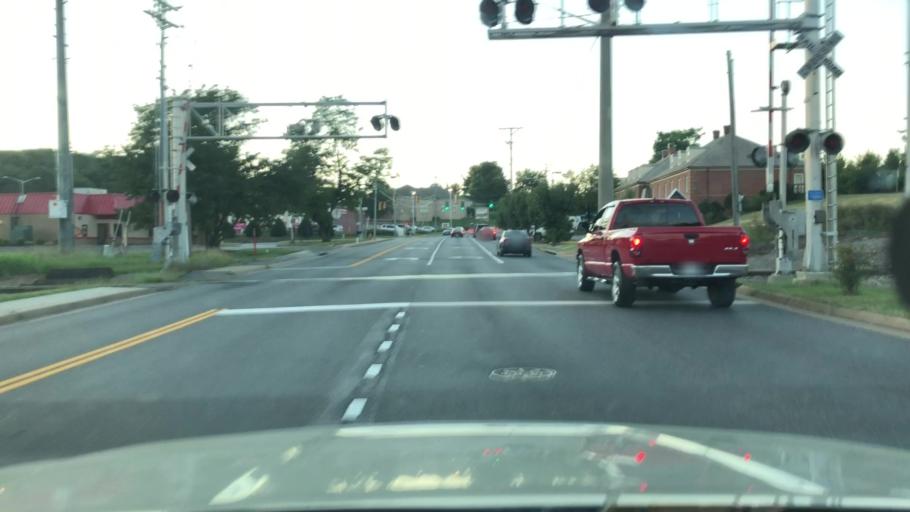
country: US
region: Virginia
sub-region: City of Harrisonburg
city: Harrisonburg
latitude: 38.4399
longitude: -78.8565
